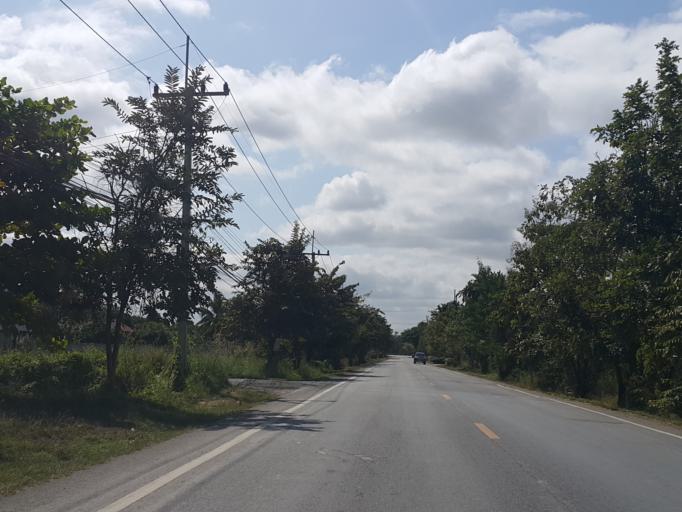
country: TH
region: Lamphun
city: Ban Thi
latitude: 18.6807
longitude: 99.1504
